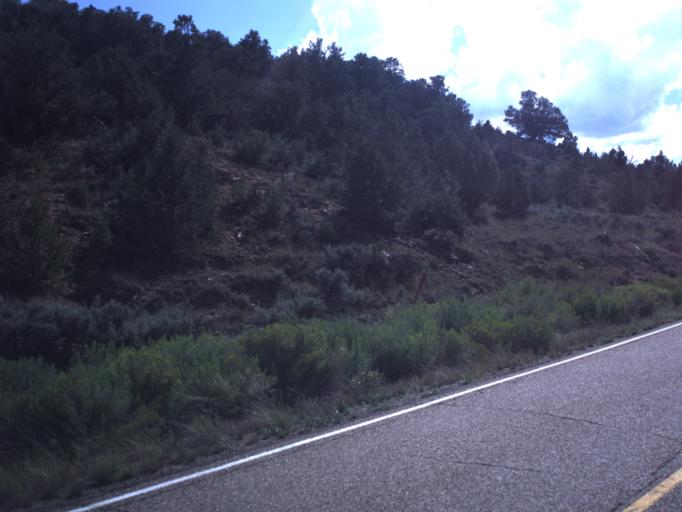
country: US
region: Utah
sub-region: Duchesne County
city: Duchesne
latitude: 40.3211
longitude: -110.6911
